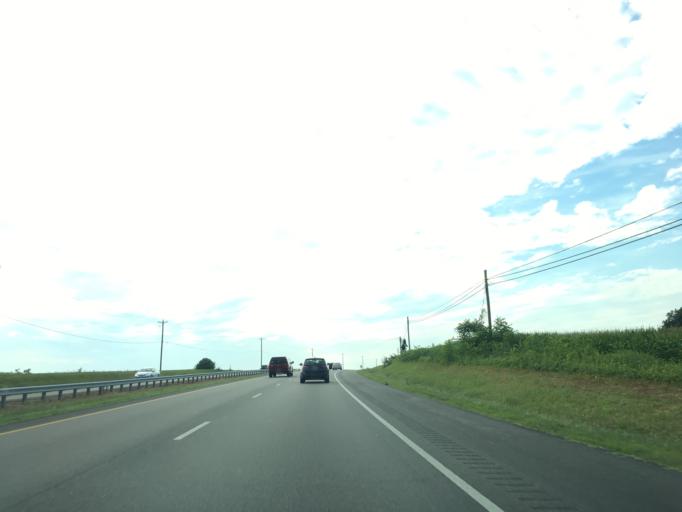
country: US
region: Maryland
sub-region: Queen Anne's County
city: Centreville
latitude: 38.9664
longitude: -76.1140
